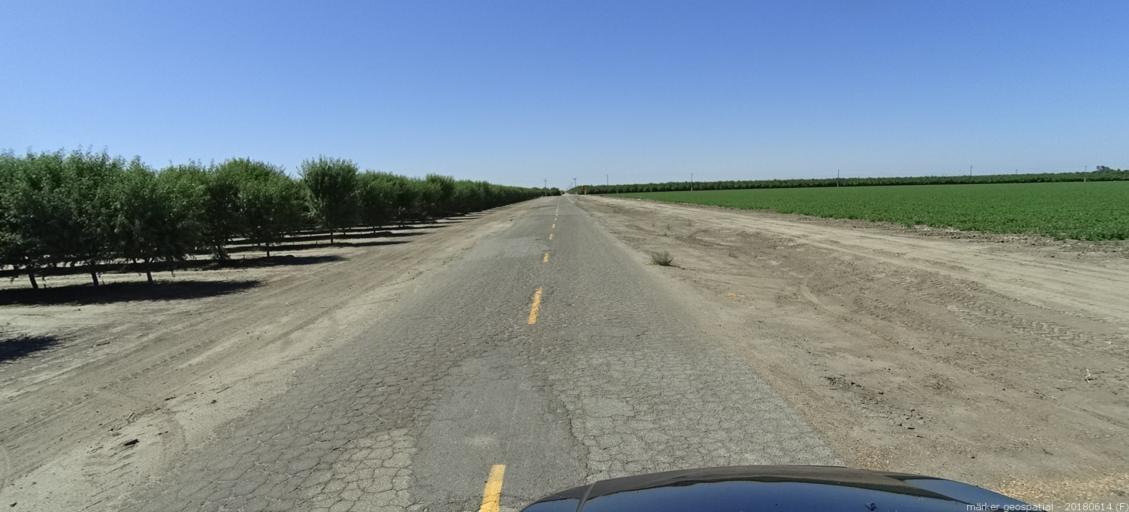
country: US
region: California
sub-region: Madera County
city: Fairmead
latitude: 36.9556
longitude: -120.2201
